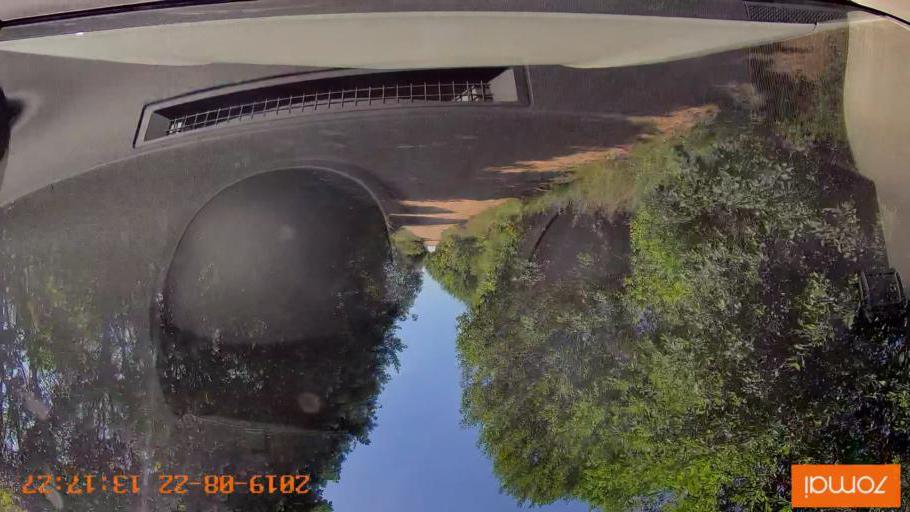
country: BY
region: Minsk
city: Prawdzinski
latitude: 53.2480
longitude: 27.9225
